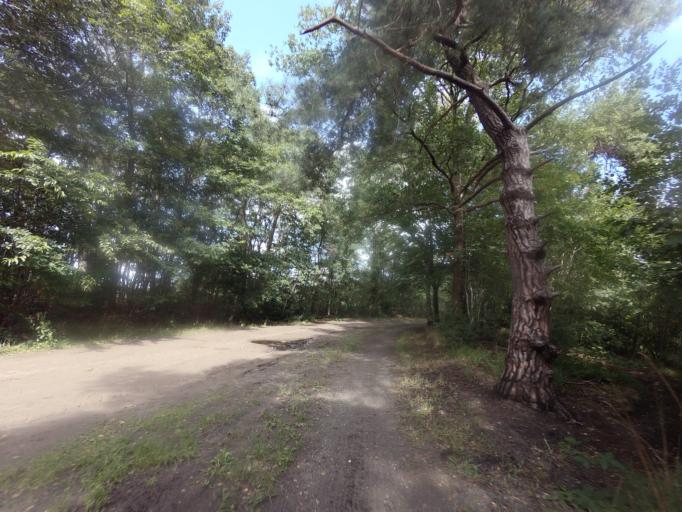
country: NL
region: Overijssel
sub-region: Gemeente Staphorst
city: Staphorst
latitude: 52.6583
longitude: 6.2626
